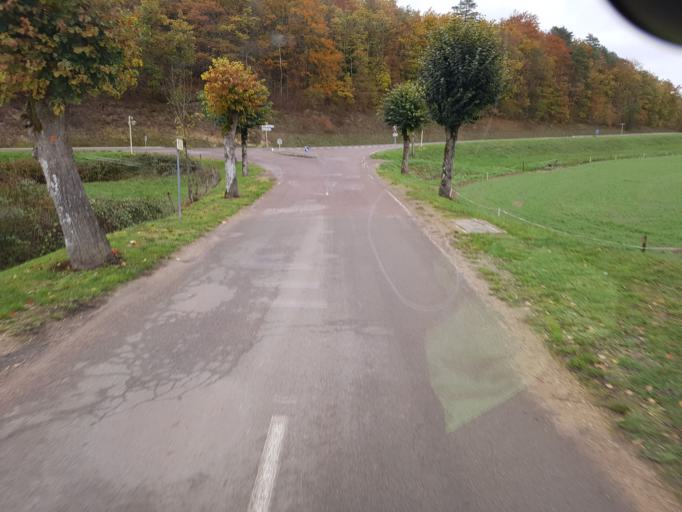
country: FR
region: Bourgogne
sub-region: Departement de la Cote-d'Or
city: Is-sur-Tille
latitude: 47.5329
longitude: 4.9885
